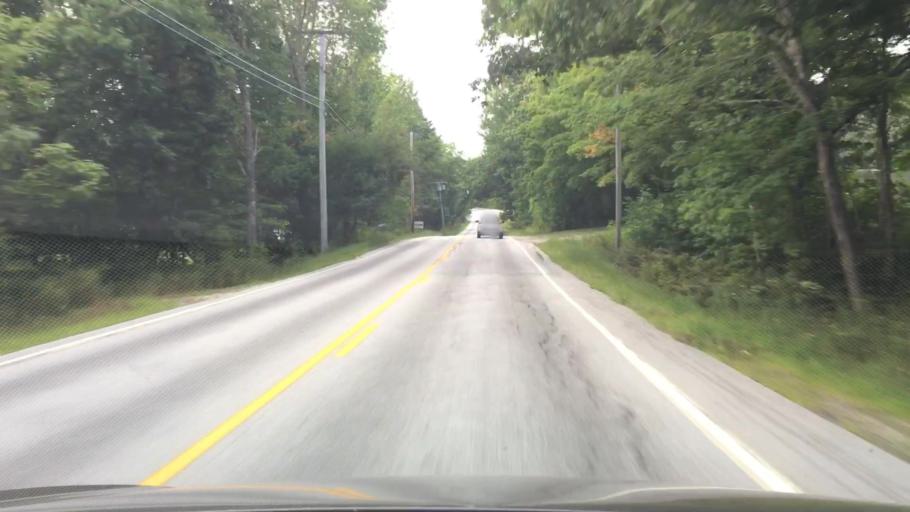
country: US
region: Maine
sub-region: Hancock County
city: Penobscot
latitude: 44.4332
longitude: -68.6059
